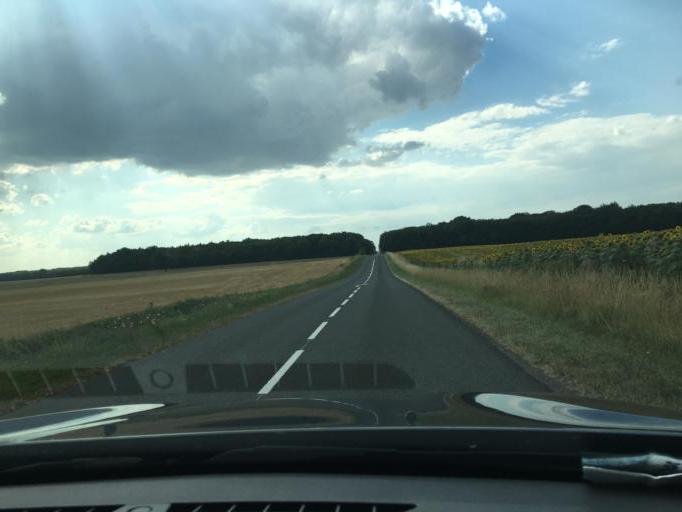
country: FR
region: Centre
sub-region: Departement du Cher
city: Baugy
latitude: 47.1001
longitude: 2.6664
